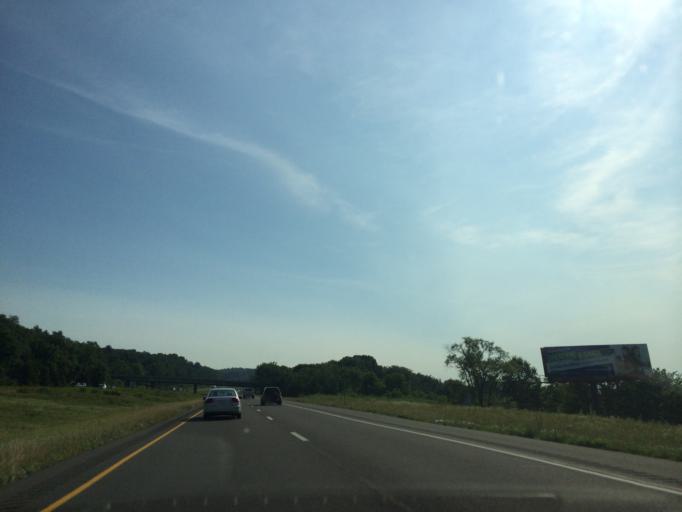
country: US
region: Pennsylvania
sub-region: Lancaster County
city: Ephrata
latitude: 40.1747
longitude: -76.1431
